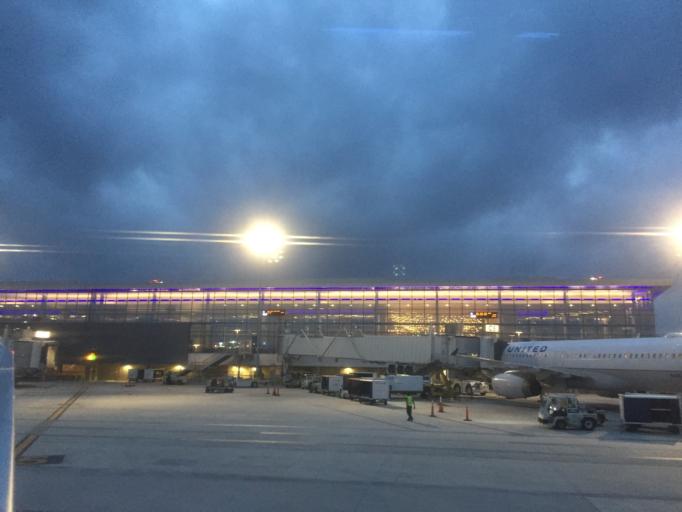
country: US
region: Texas
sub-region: Harris County
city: Aldine
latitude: 29.9893
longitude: -95.3405
